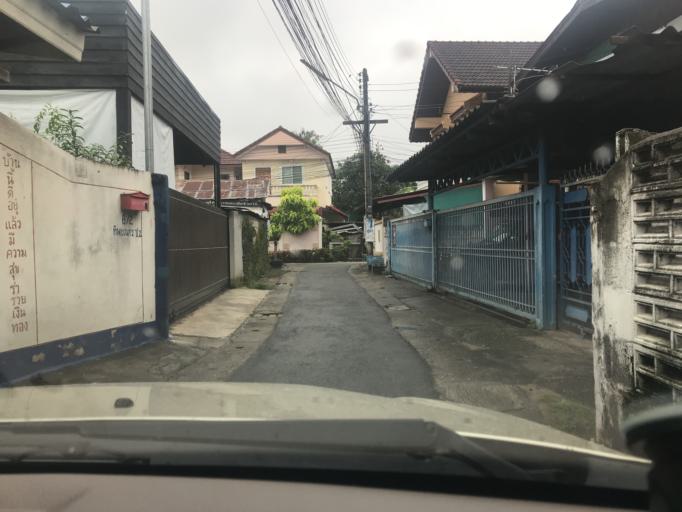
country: TH
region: Chiang Mai
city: Chiang Mai
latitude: 18.7788
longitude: 98.9819
